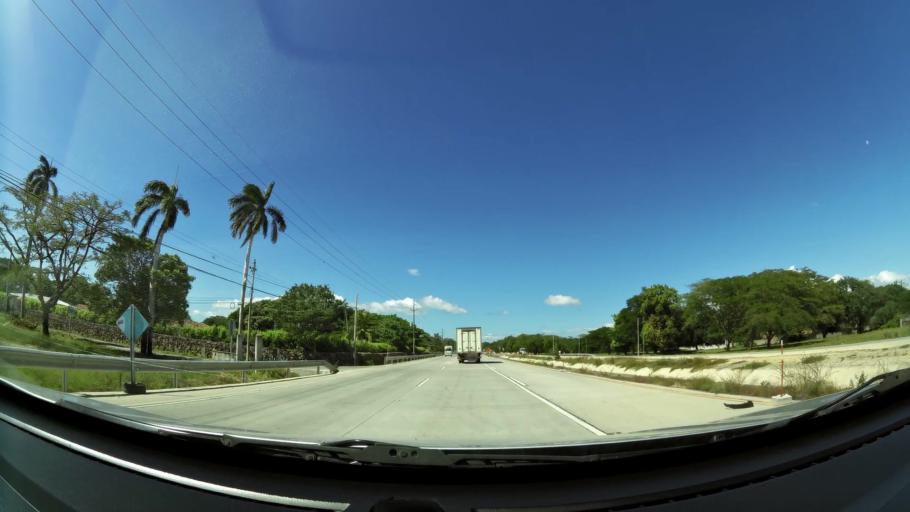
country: CR
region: Guanacaste
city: Liberia
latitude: 10.5985
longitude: -85.4256
